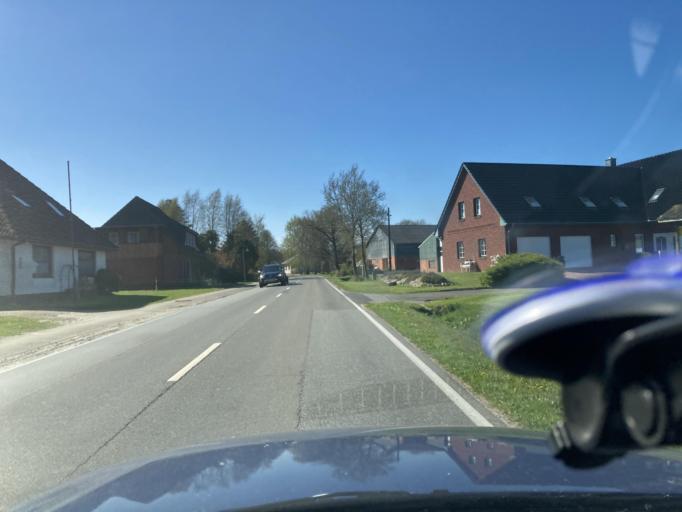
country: DE
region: Schleswig-Holstein
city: Odderade
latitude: 54.1409
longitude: 9.1908
